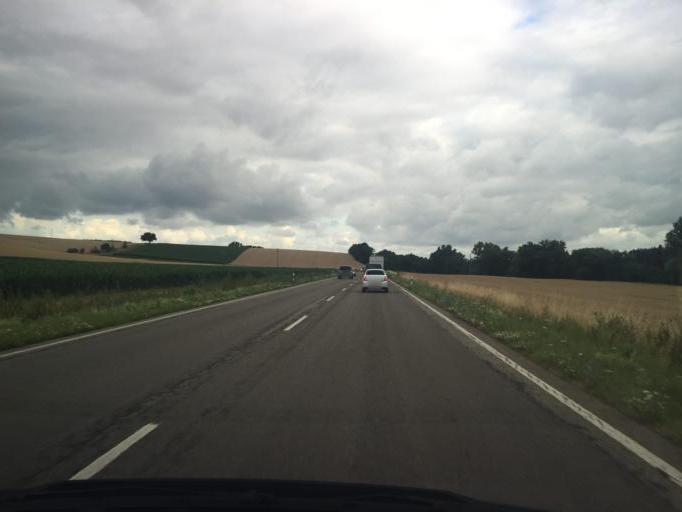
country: DE
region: Baden-Wuerttemberg
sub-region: Karlsruhe Region
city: Gondelsheim
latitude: 49.0744
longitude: 8.6559
